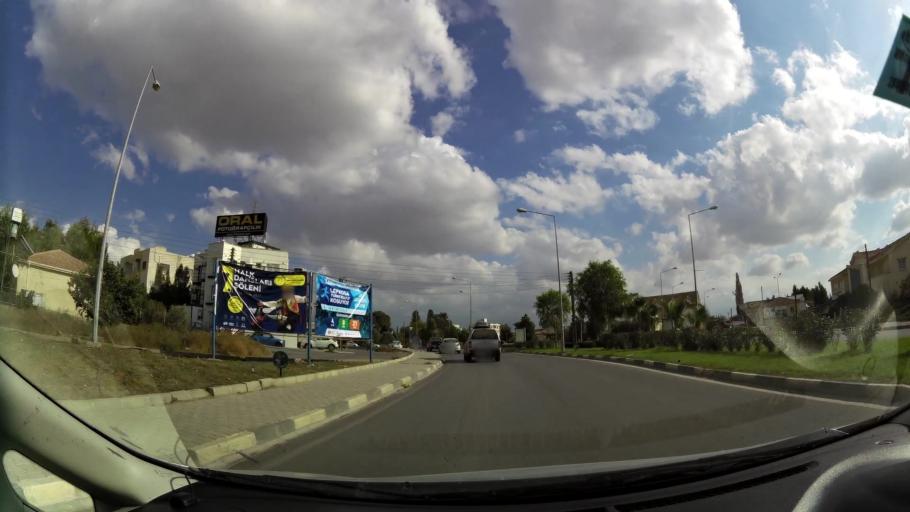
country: CY
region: Lefkosia
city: Nicosia
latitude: 35.1990
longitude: 33.3539
